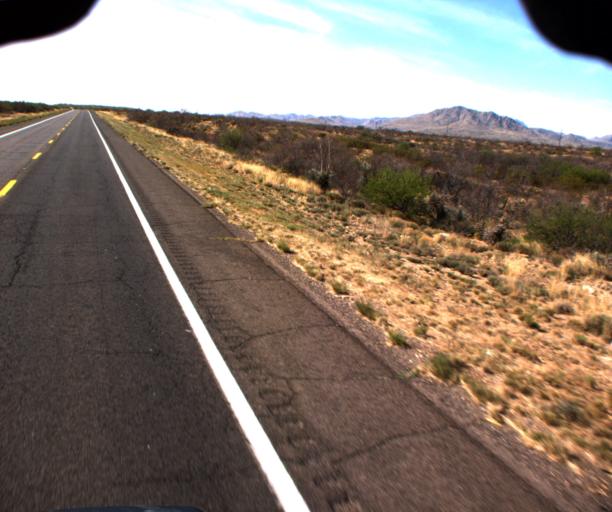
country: US
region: Arizona
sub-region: Graham County
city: Swift Trail Junction
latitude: 32.6491
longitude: -109.6977
